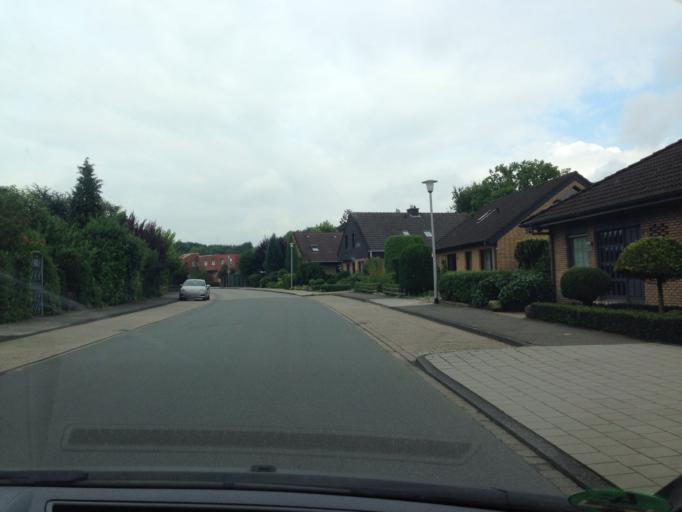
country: DE
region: North Rhine-Westphalia
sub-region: Regierungsbezirk Munster
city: Muenster
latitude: 51.9914
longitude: 7.5507
